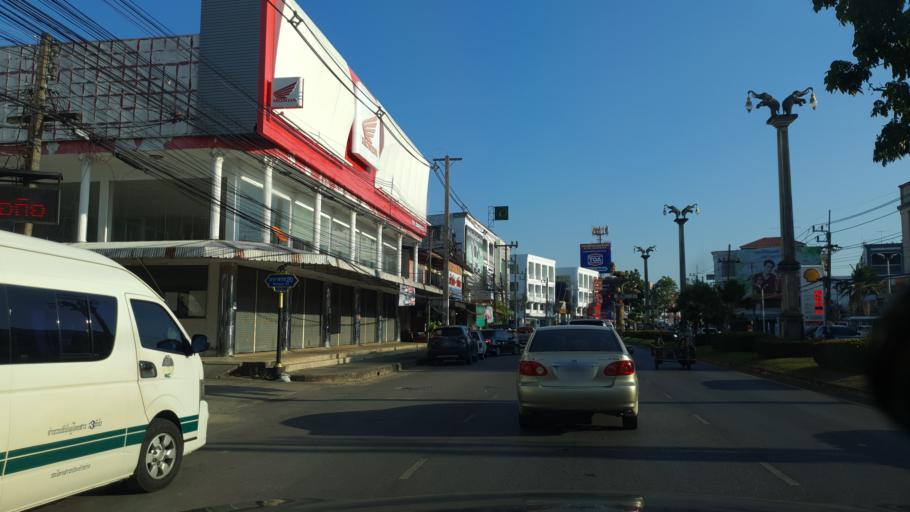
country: TH
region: Krabi
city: Krabi
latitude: 8.0673
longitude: 98.9146
